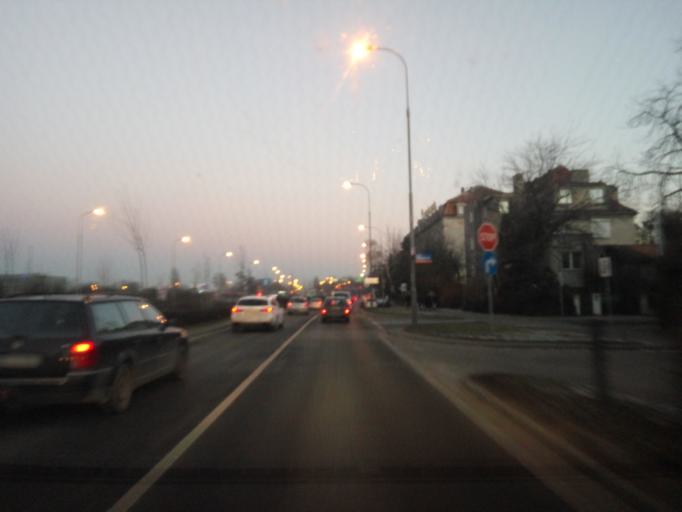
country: PL
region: Lower Silesian Voivodeship
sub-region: Powiat wroclawski
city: Wroclaw
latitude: 51.0846
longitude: 17.0207
